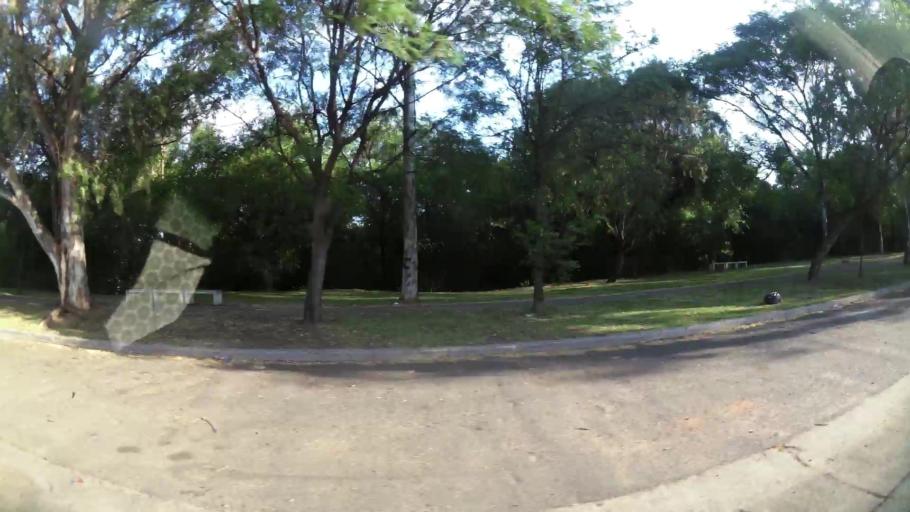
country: AR
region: Cordoba
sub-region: Departamento de Capital
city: Cordoba
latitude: -31.3938
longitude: -64.2174
